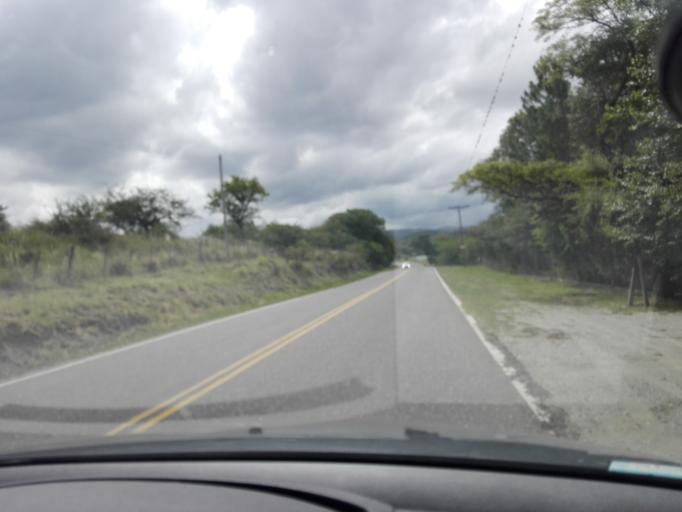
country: AR
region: Cordoba
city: Alta Gracia
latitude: -31.5868
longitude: -64.4749
